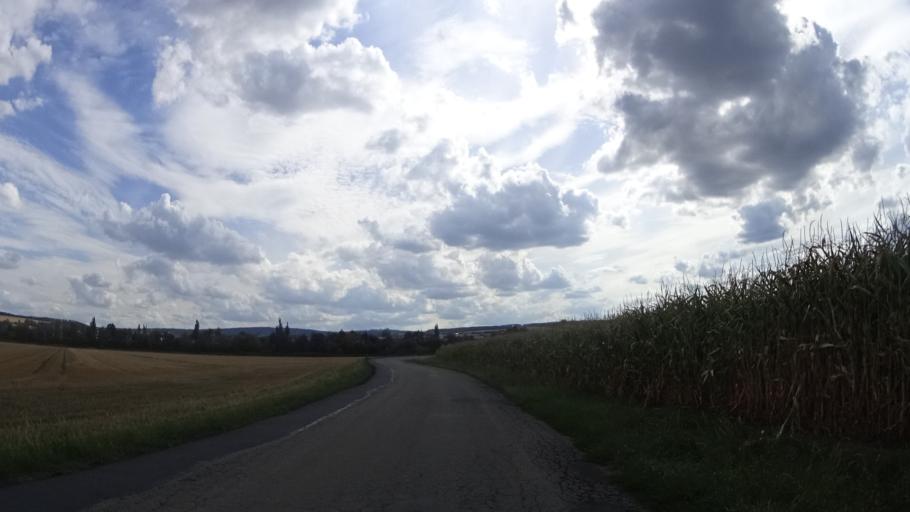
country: CZ
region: Olomoucky
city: Bila Lhota
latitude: 49.7304
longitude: 16.9847
